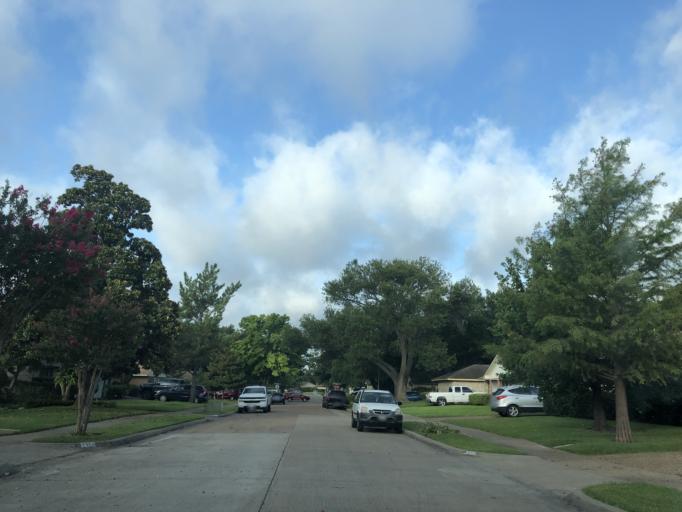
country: US
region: Texas
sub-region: Dallas County
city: Garland
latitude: 32.8519
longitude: -96.6361
